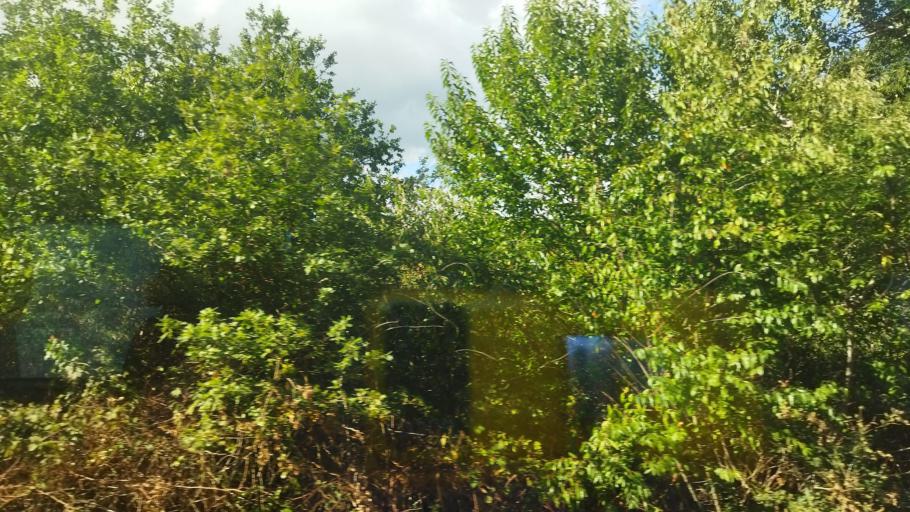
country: DE
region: Lower Saxony
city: Lingen
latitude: 52.5309
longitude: 7.3298
